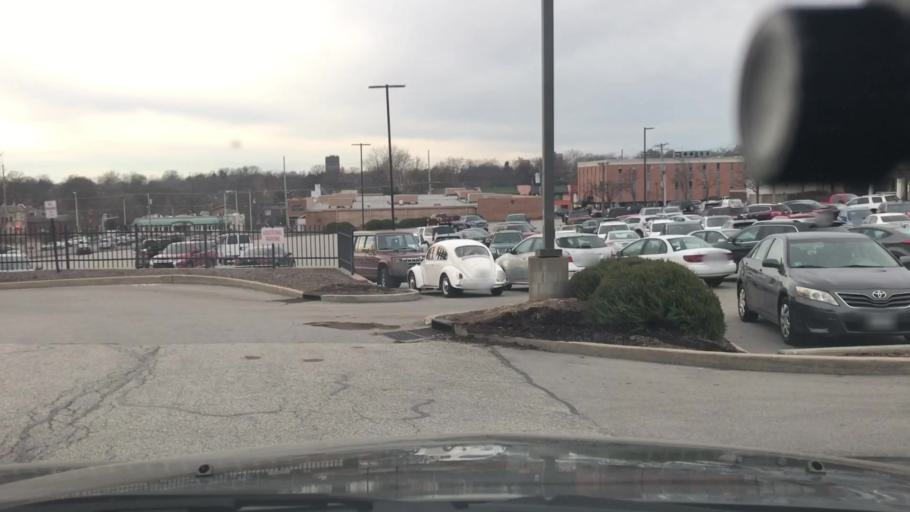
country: US
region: Missouri
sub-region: Saint Louis County
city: Richmond Heights
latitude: 38.6334
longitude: -90.3164
